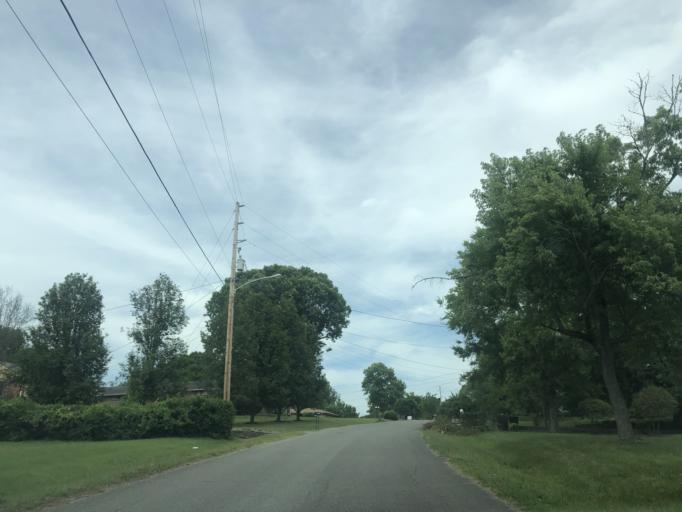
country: US
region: Tennessee
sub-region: Davidson County
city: Nashville
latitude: 36.2152
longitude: -86.8057
